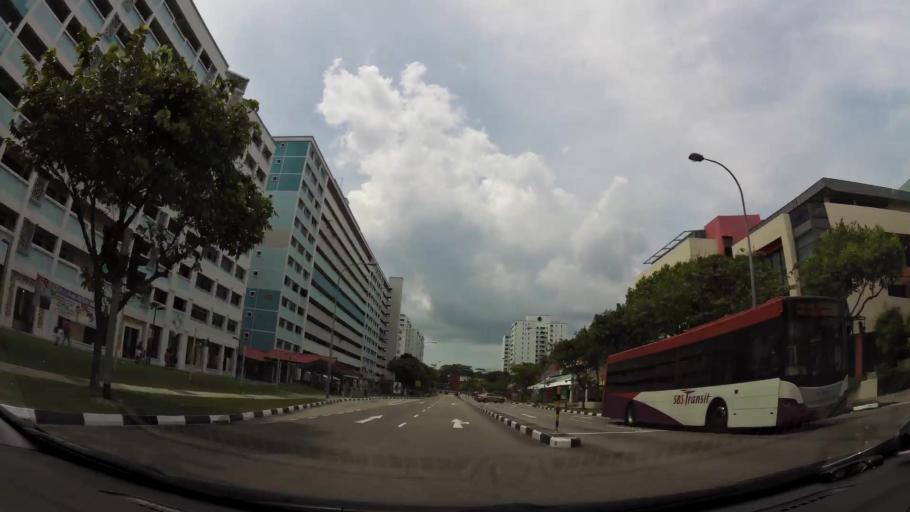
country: MY
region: Johor
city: Johor Bahru
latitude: 1.3482
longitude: 103.6990
